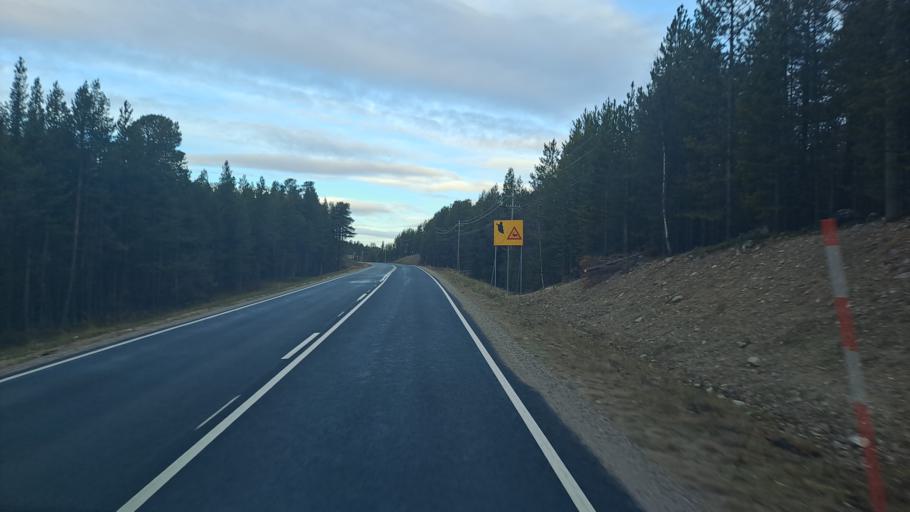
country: FI
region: Lapland
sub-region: Pohjois-Lappi
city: Inari
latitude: 68.9127
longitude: 27.0041
